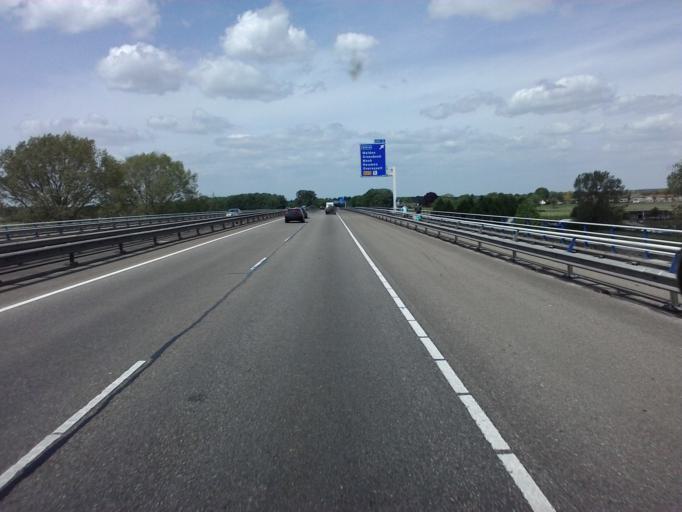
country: NL
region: North Brabant
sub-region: Gemeente Cuijk
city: Cuijk
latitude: 51.7583
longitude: 5.8386
